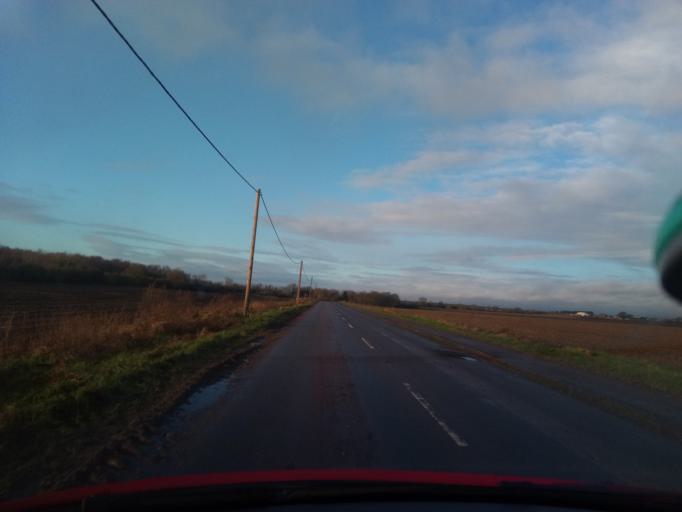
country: GB
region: England
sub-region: Derbyshire
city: Melbourne
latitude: 52.8499
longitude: -1.4190
